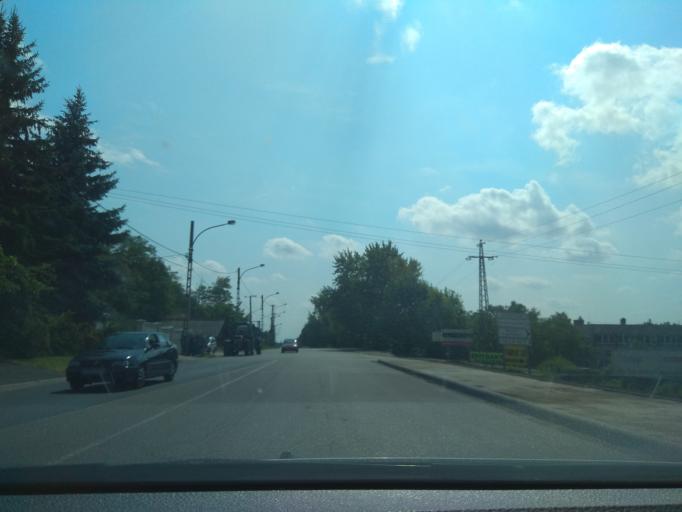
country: HU
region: Heves
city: Eger
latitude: 47.8812
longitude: 20.3991
